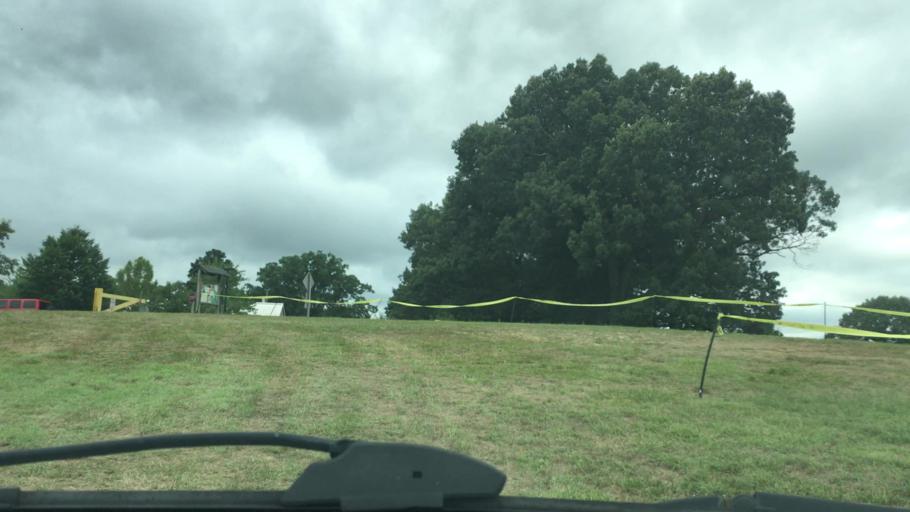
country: US
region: Maryland
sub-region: Anne Arundel County
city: Pasadena
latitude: 39.1008
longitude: -76.5811
